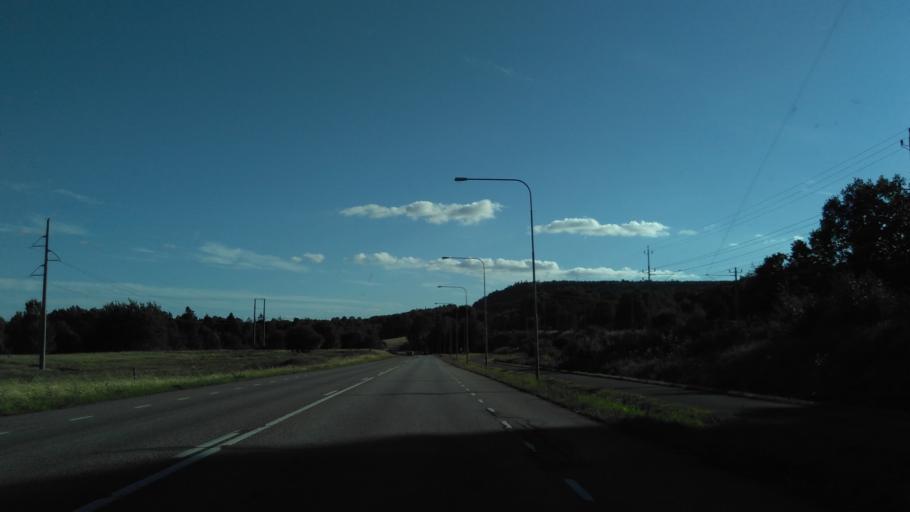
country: SE
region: Vaestra Goetaland
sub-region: Skovde Kommun
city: Skultorp
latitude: 58.3621
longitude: 13.8308
